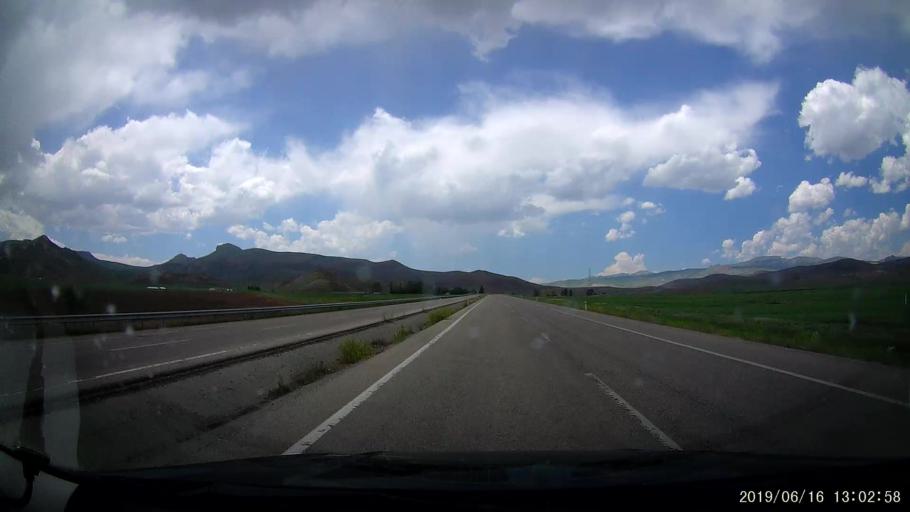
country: TR
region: Agri
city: Sulucem
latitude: 39.5777
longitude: 43.8018
